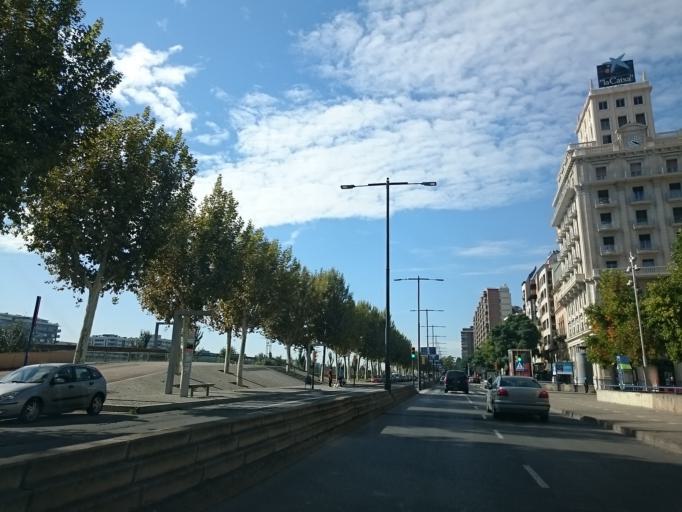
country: ES
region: Catalonia
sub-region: Provincia de Lleida
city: Lleida
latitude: 41.6132
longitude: 0.6254
